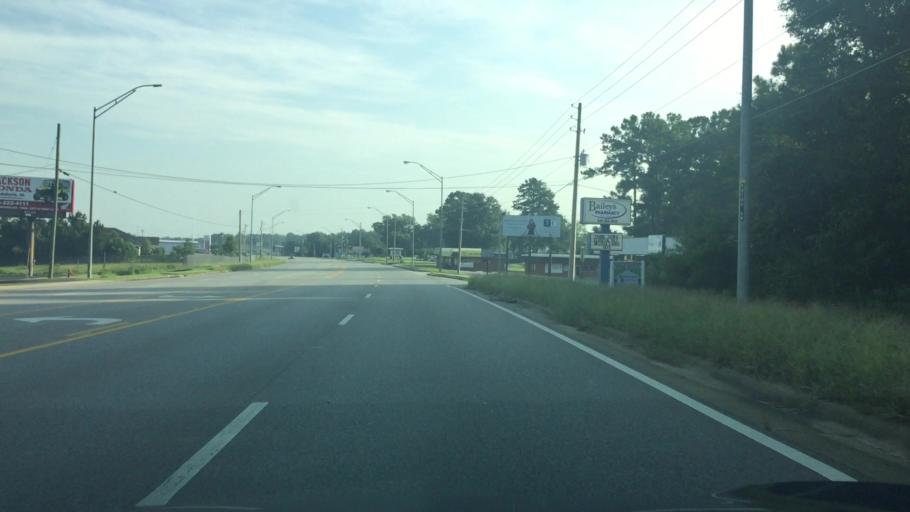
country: US
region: Alabama
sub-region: Covington County
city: Andalusia
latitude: 31.2986
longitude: -86.4996
